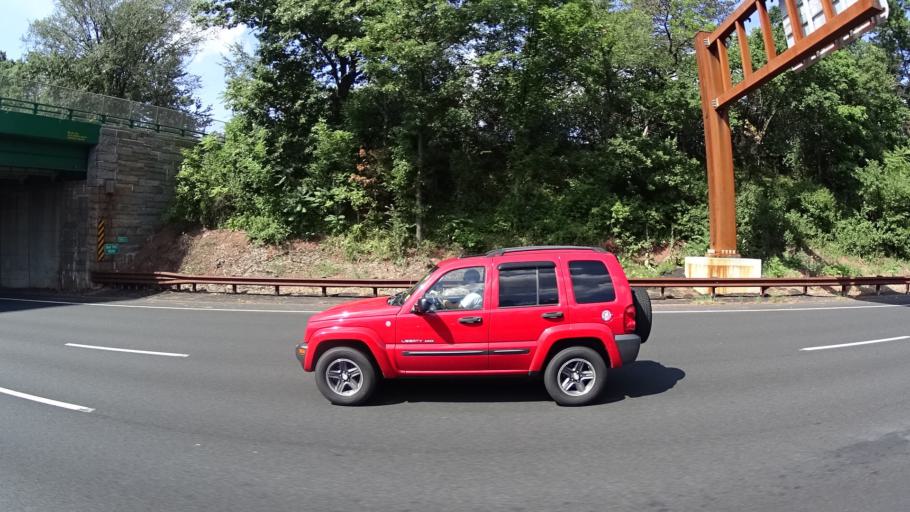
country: US
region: New Jersey
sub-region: Middlesex County
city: Iselin
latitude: 40.5737
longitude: -74.3303
